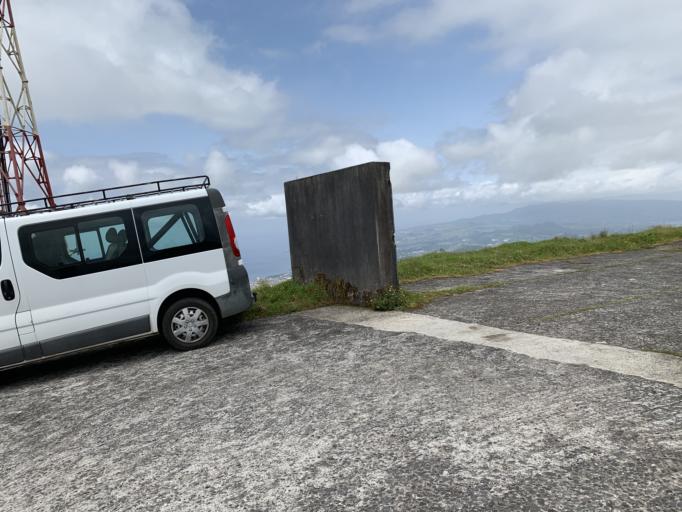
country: PT
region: Azores
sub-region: Vila Franca do Campo
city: Vila Franca do Campo
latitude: 37.7599
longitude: -25.4915
